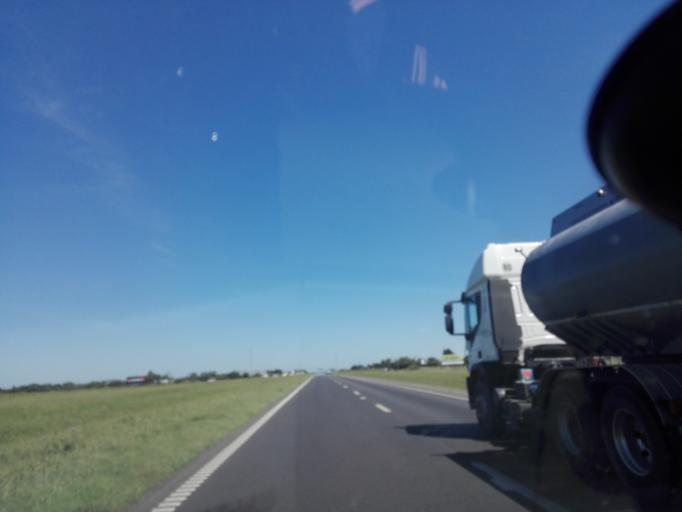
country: AR
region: Buenos Aires
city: San Nicolas de los Arroyos
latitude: -33.3749
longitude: -60.2407
